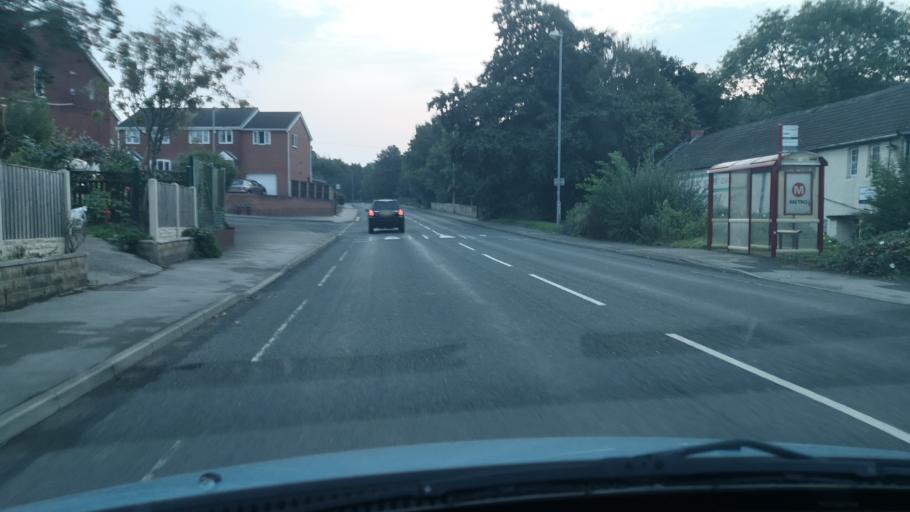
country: GB
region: England
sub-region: City and Borough of Wakefield
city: North Elmsall
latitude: 53.6147
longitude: -1.2796
